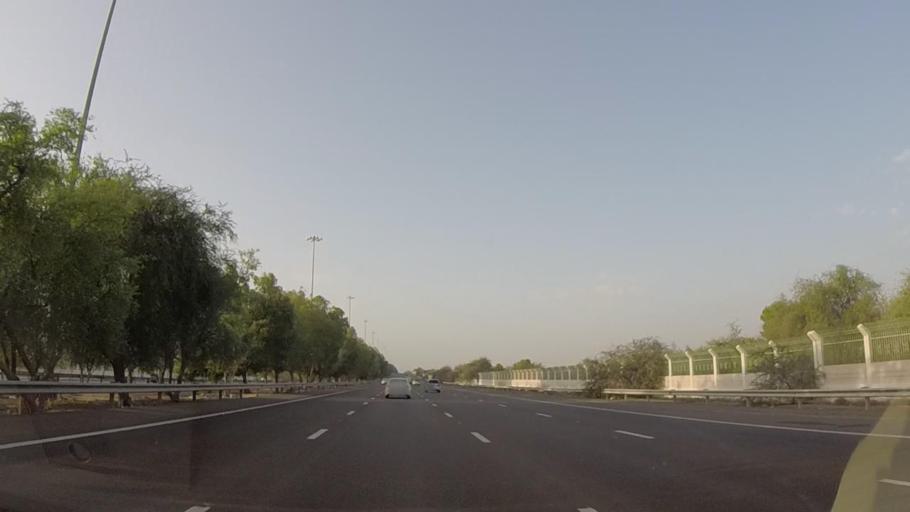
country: AE
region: Dubai
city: Dubai
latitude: 24.8414
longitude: 54.8903
